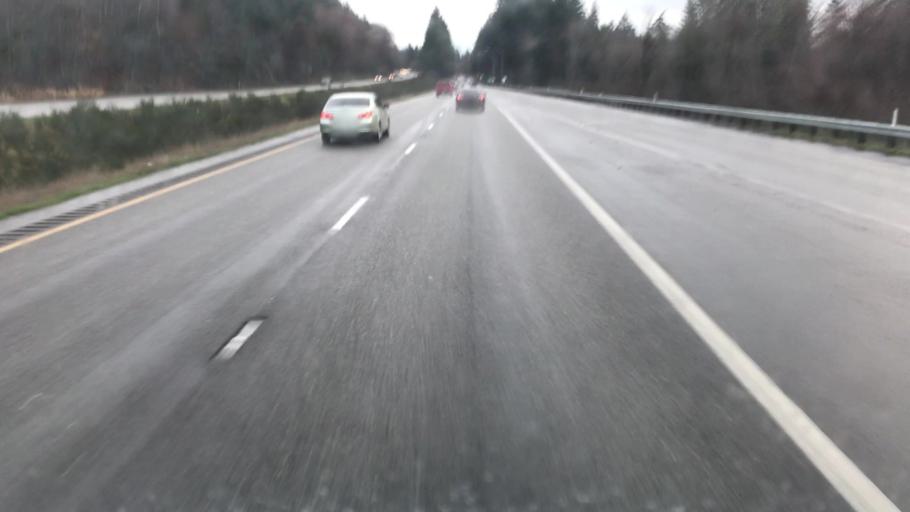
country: US
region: Washington
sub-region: Kitsap County
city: Burley
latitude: 47.4299
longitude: -122.6236
